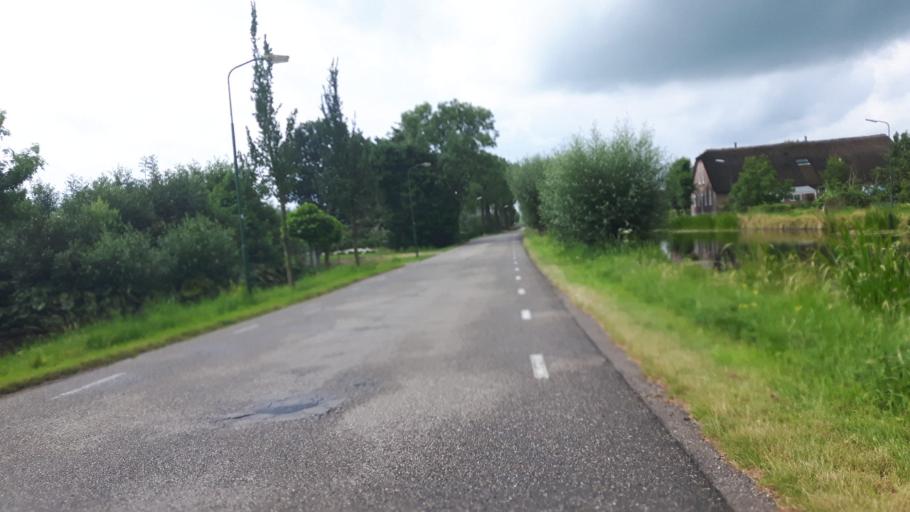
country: NL
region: South Holland
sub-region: Gemeente Schoonhoven
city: Schoonhoven
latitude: 51.9805
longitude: 4.8611
